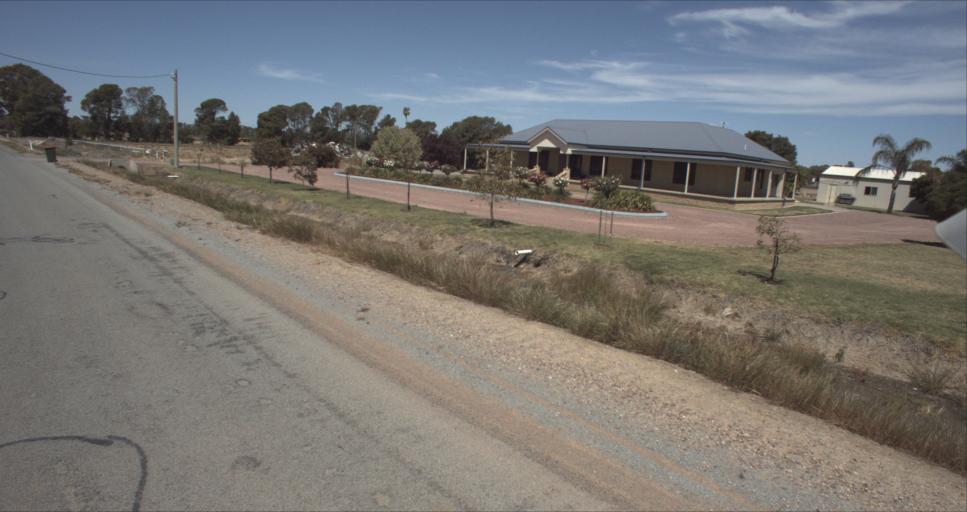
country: AU
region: New South Wales
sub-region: Leeton
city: Leeton
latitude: -34.5725
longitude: 146.4200
